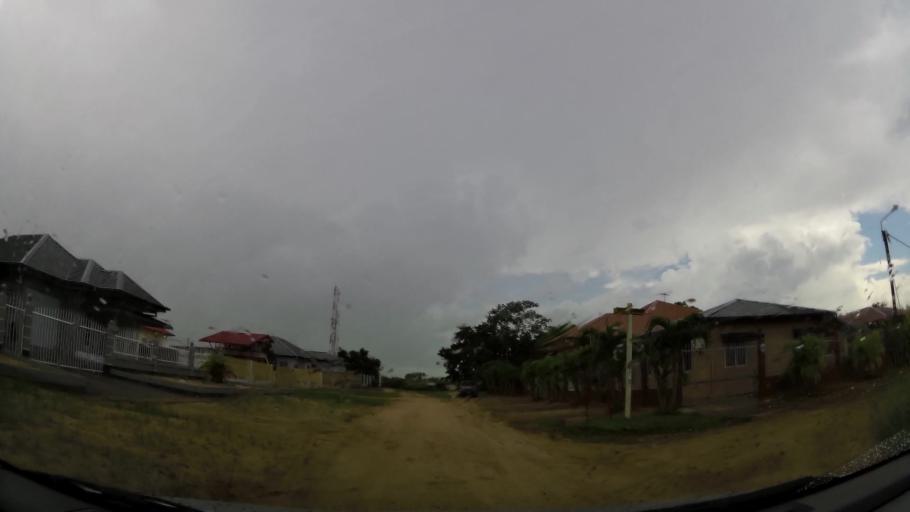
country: SR
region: Commewijne
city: Nieuw Amsterdam
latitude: 5.8526
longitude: -55.1170
